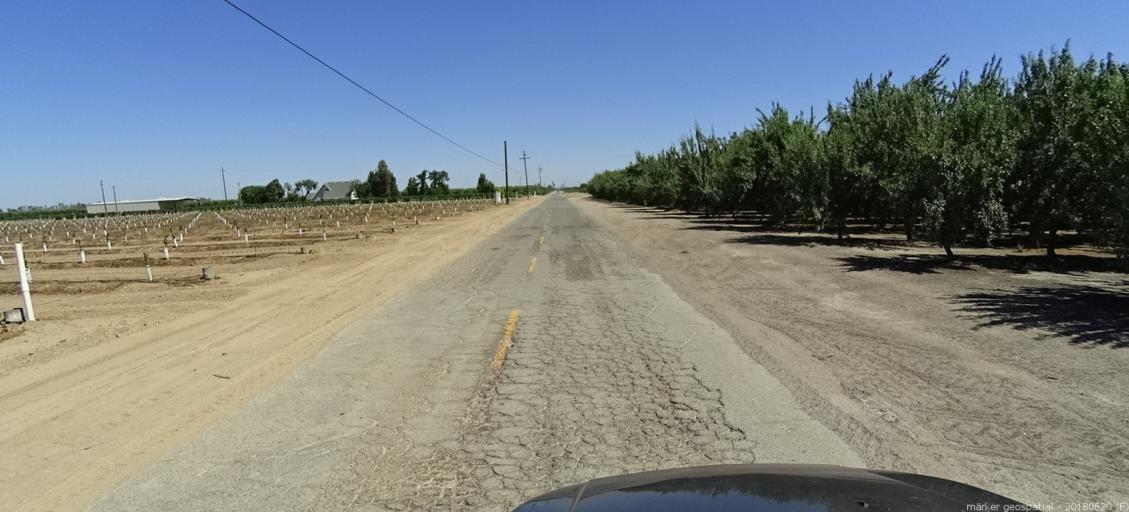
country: US
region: California
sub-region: Madera County
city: Parkwood
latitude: 36.8972
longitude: -120.0105
